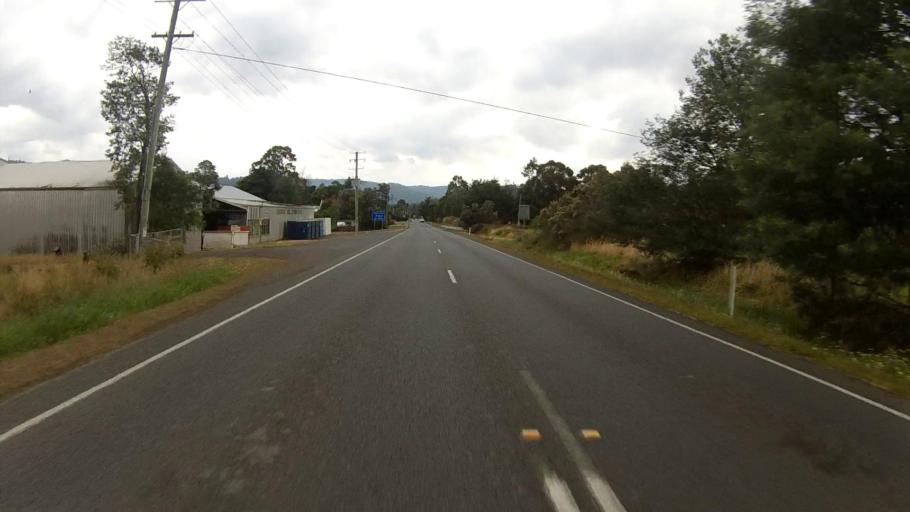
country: AU
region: Tasmania
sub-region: Huon Valley
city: Franklin
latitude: -43.1084
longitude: 147.0353
